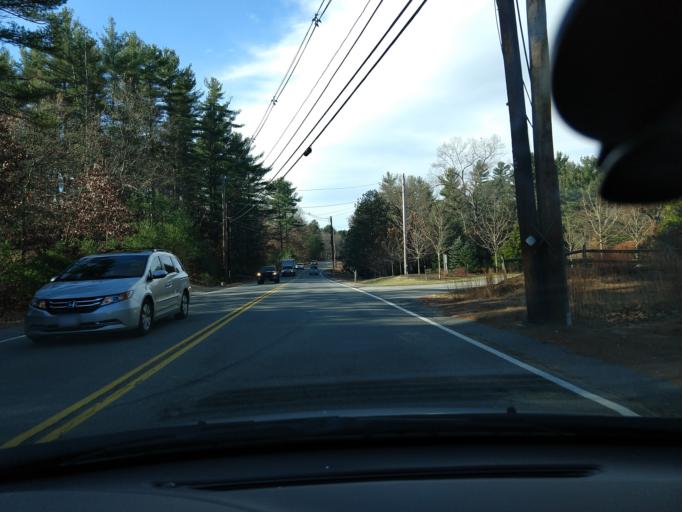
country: US
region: Massachusetts
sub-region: Middlesex County
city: Dunstable
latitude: 42.6712
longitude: -71.5045
